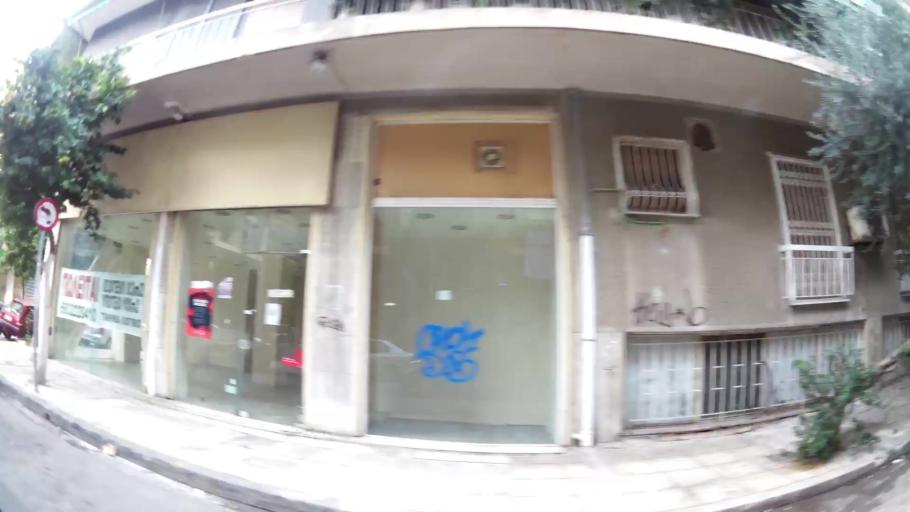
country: GR
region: Attica
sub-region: Nomarchia Athinas
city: Kallithea
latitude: 37.9480
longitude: 23.6958
